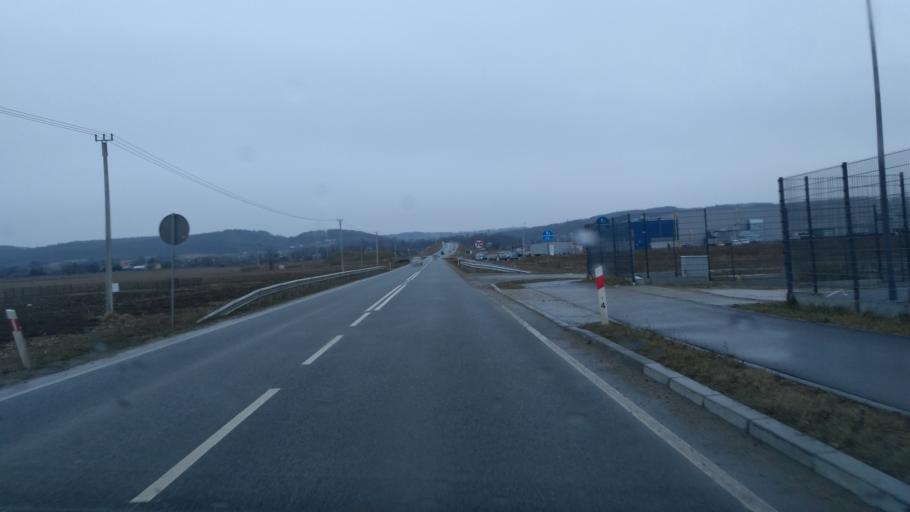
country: PL
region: Subcarpathian Voivodeship
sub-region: Powiat debicki
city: Brzeznica
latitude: 50.0712
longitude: 21.4709
